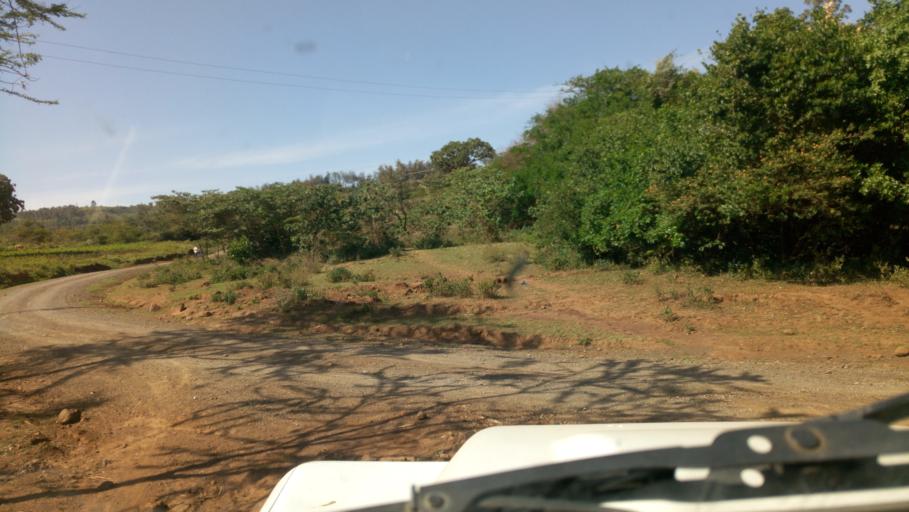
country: KE
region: Nakuru
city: Nakuru
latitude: -0.1415
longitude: 36.0168
